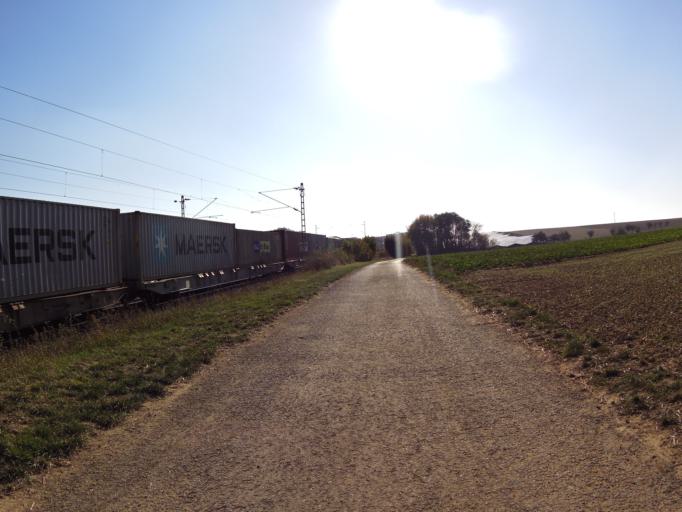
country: DE
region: Bavaria
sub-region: Regierungsbezirk Unterfranken
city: Reichenberg
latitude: 49.7044
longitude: 9.9277
